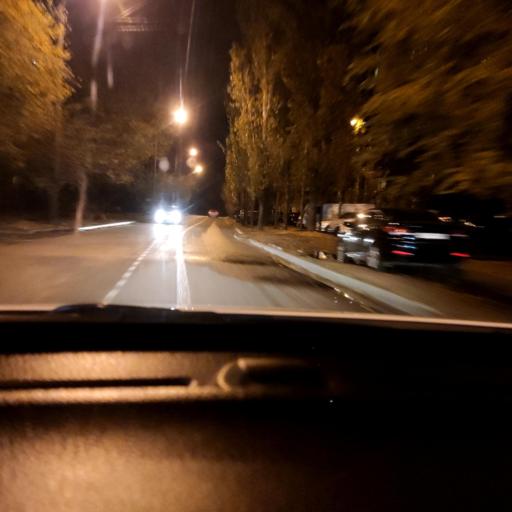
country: RU
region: Voronezj
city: Maslovka
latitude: 51.6327
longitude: 39.2849
